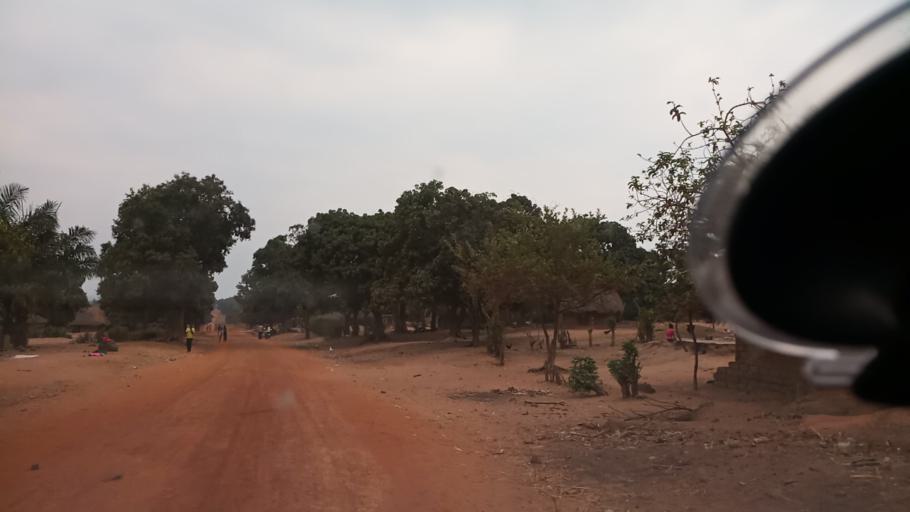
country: ZM
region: Luapula
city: Nchelenge
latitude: -9.1829
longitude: 28.2831
